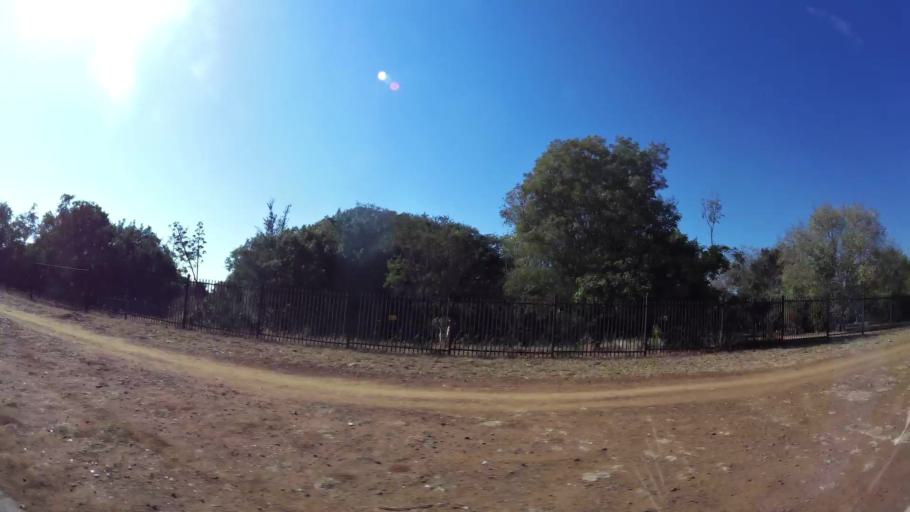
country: ZA
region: Gauteng
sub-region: City of Tshwane Metropolitan Municipality
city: Pretoria
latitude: -25.6703
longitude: 28.2379
